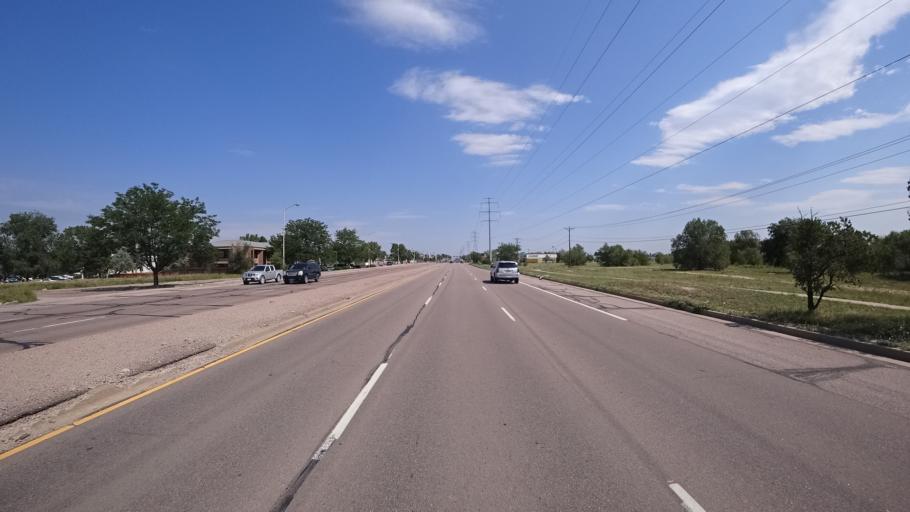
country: US
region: Colorado
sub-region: El Paso County
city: Stratmoor
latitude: 38.8015
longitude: -104.7575
